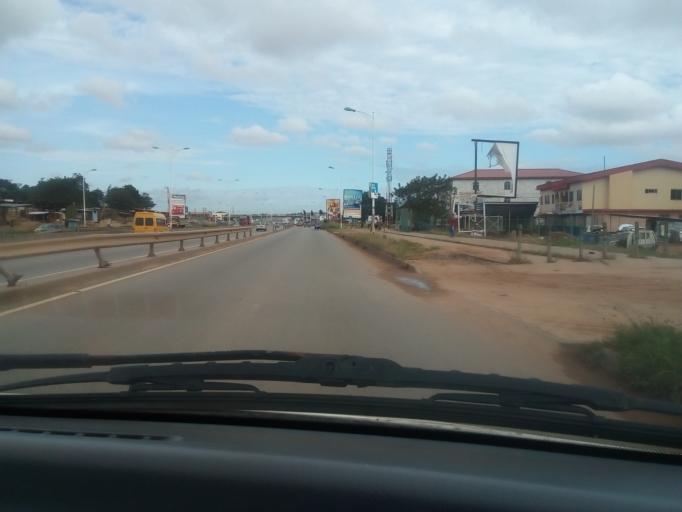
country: GH
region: Greater Accra
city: Dome
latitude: 5.6557
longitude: -0.2627
